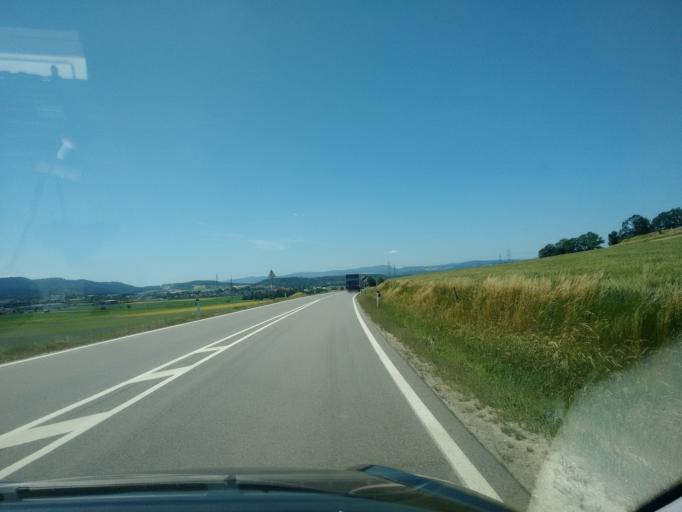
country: AT
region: Lower Austria
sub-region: Politischer Bezirk Sankt Polten
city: Haunoldstein
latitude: 48.1936
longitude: 15.4304
